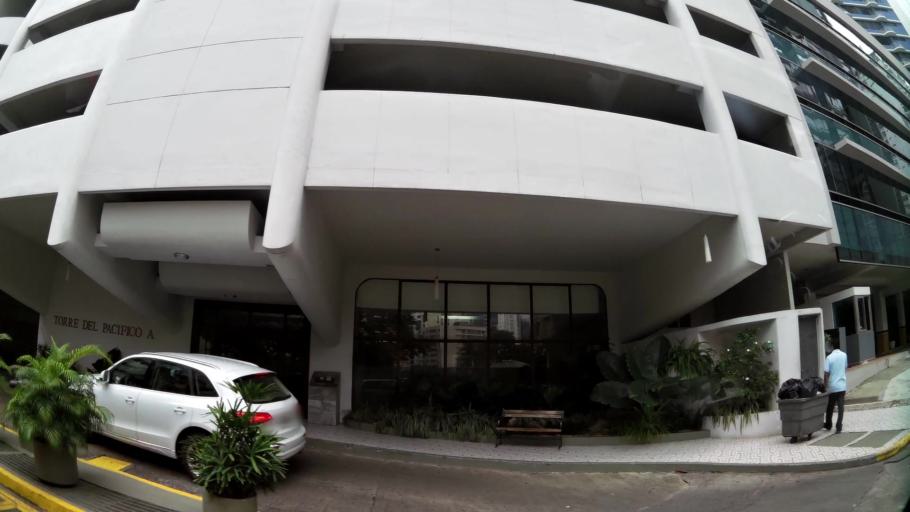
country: PA
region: Panama
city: Panama
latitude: 8.9766
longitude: -79.5193
